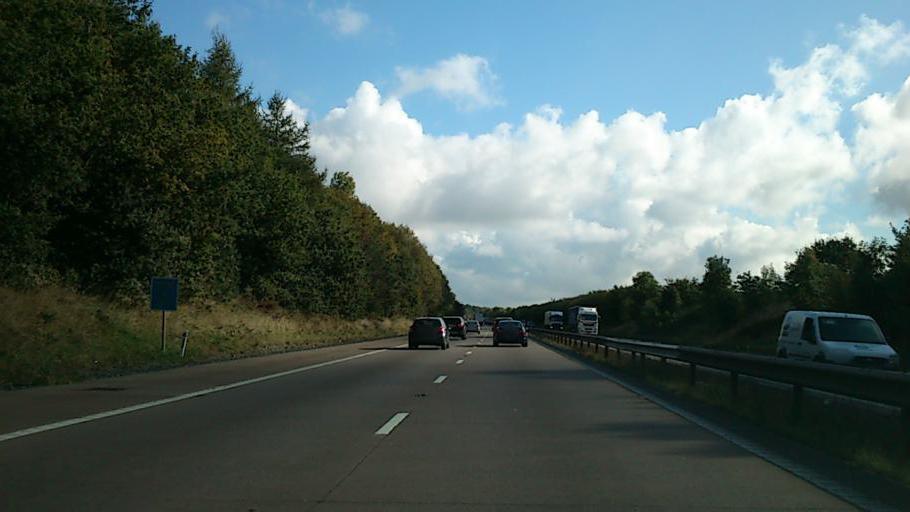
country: GB
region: England
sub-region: Shropshire
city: Albrighton
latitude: 52.6507
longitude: -2.2547
